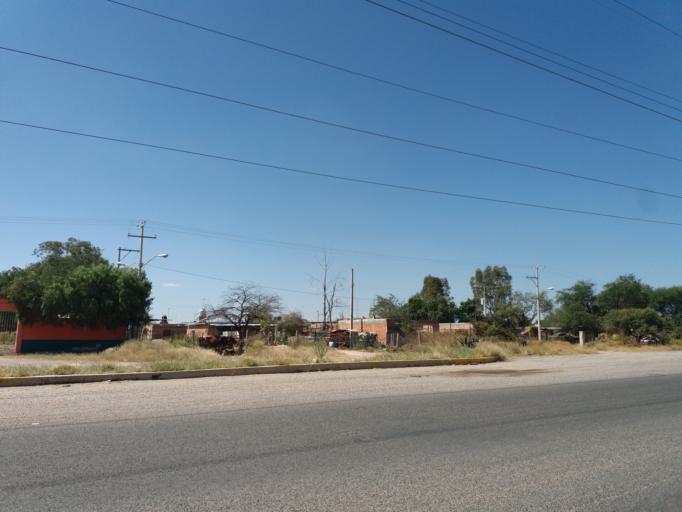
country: MX
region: Aguascalientes
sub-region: Aguascalientes
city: San Sebastian [Fraccionamiento]
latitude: 21.8115
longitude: -102.2923
